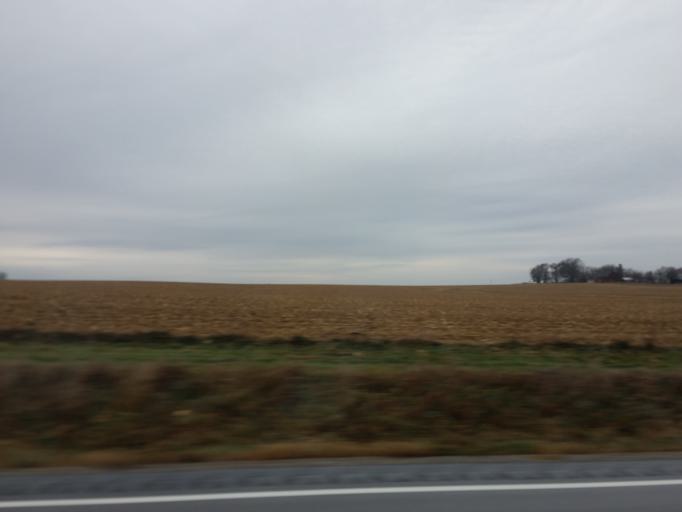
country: US
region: Iowa
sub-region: Benton County
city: Vinton
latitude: 42.0192
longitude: -92.0292
